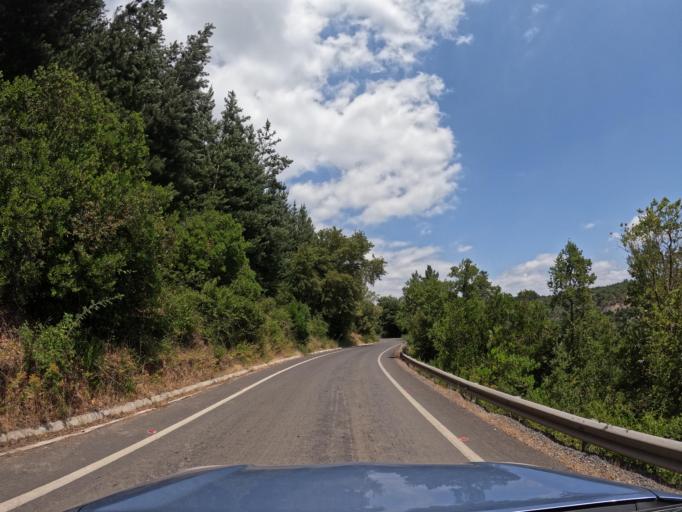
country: CL
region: Maule
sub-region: Provincia de Curico
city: Molina
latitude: -35.1783
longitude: -71.0834
